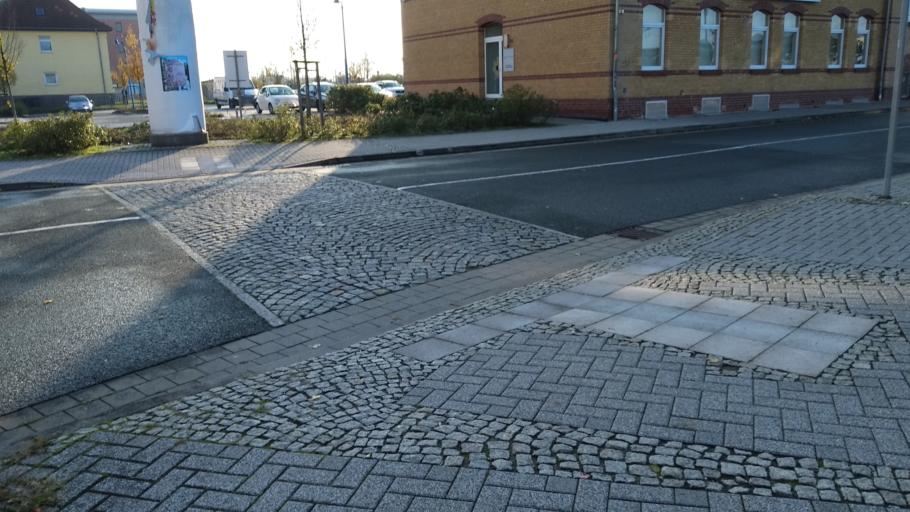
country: DE
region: Saxony
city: Bitterfeld-Wolfen
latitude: 51.6222
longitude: 12.3181
